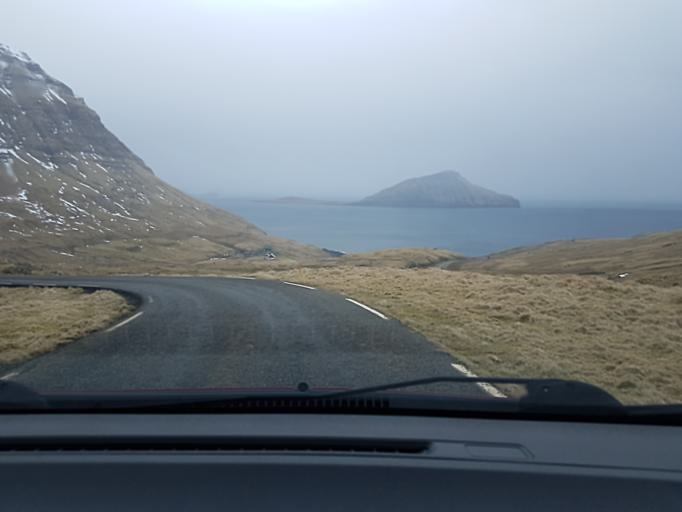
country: FO
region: Streymoy
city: Kollafjordhur
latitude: 62.0482
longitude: -6.9230
